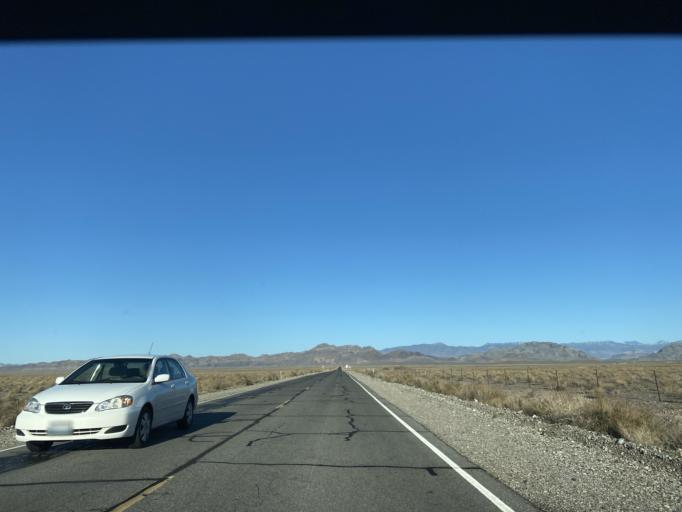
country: US
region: Nevada
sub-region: Nye County
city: Pahrump
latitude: 36.3402
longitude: -116.3381
